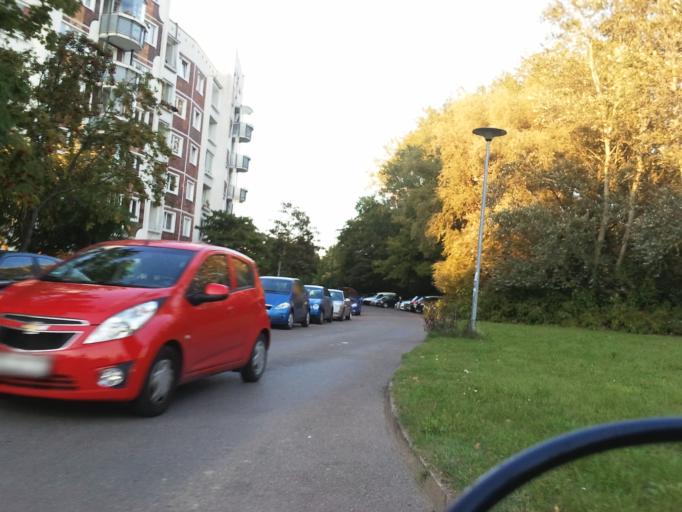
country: DE
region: Mecklenburg-Vorpommern
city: Warnemuende
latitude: 54.1268
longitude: 12.0691
